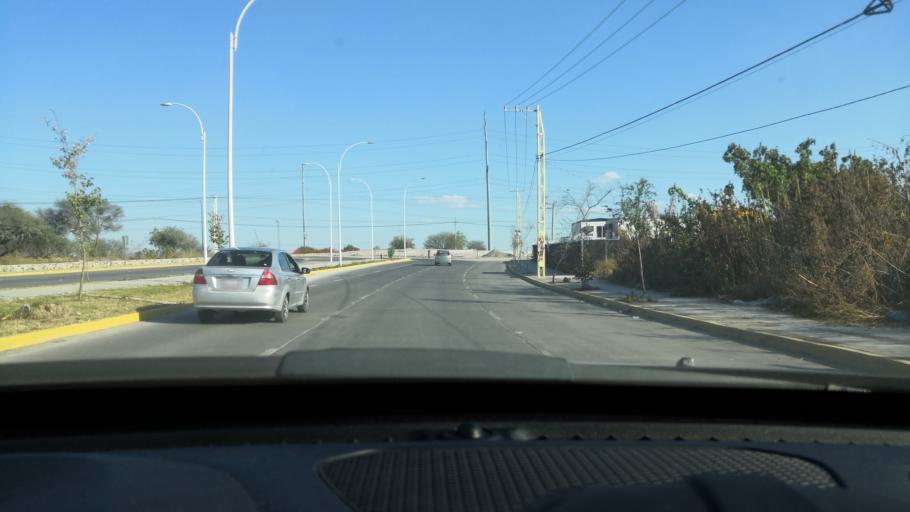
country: MX
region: Guanajuato
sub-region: Leon
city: Fraccionamiento Paraiso Real
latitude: 21.0594
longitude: -101.6101
